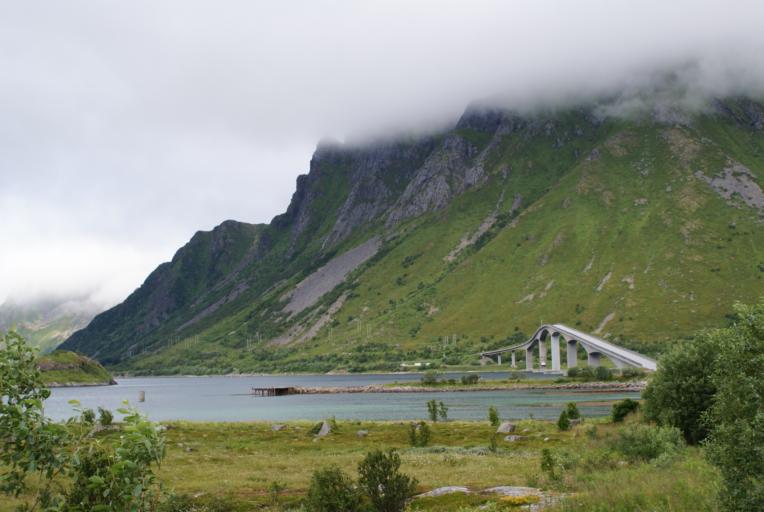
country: NO
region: Nordland
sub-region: Vagan
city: Kabelvag
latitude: 68.2602
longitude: 14.2713
